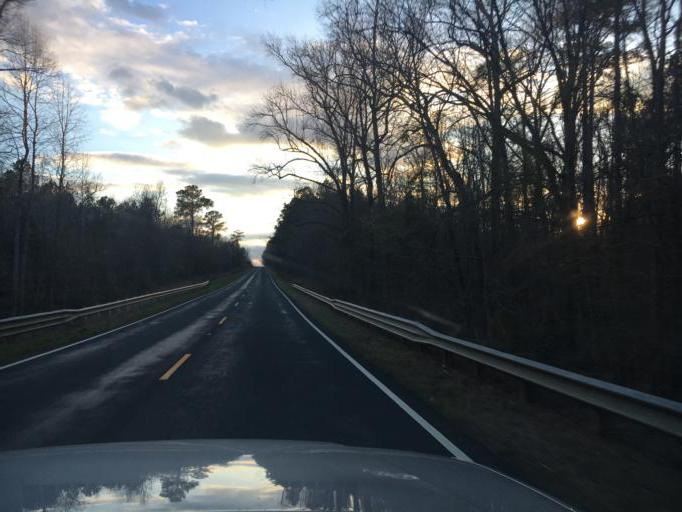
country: US
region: South Carolina
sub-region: Greenwood County
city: Greenwood
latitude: 34.0864
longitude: -82.2029
